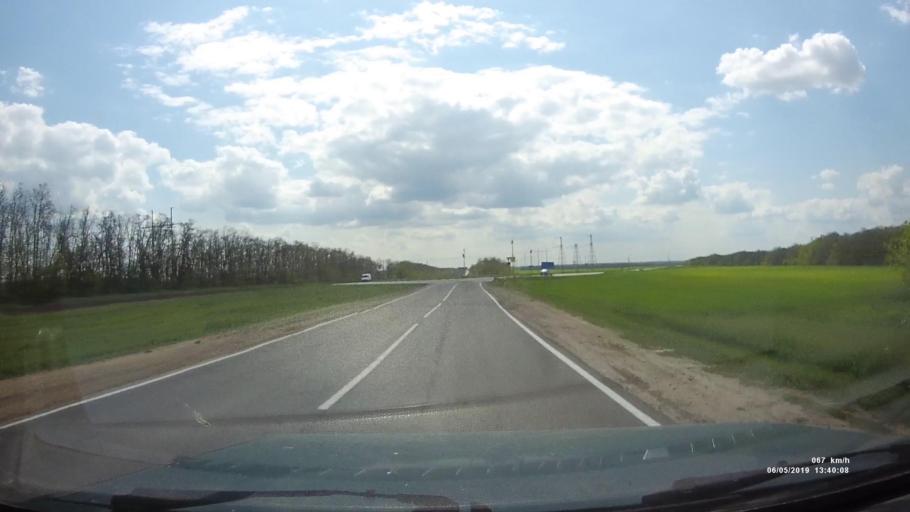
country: RU
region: Rostov
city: Ust'-Donetskiy
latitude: 47.6685
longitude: 40.6967
